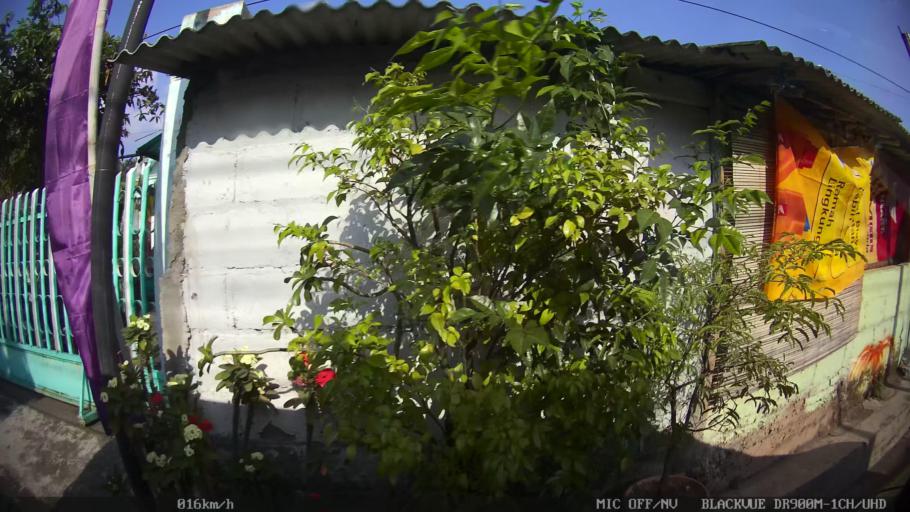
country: ID
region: Daerah Istimewa Yogyakarta
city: Yogyakarta
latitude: -7.7985
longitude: 110.3492
